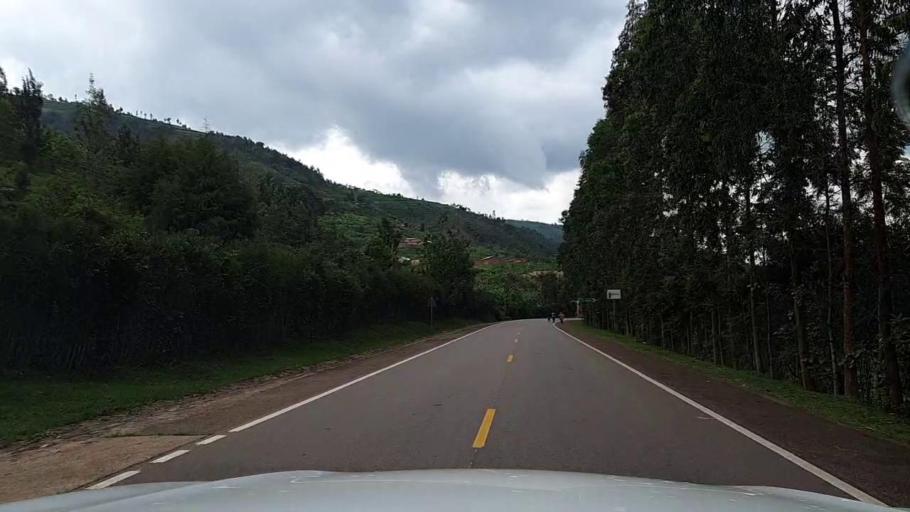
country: RW
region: Northern Province
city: Byumba
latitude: -1.6812
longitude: 30.1029
